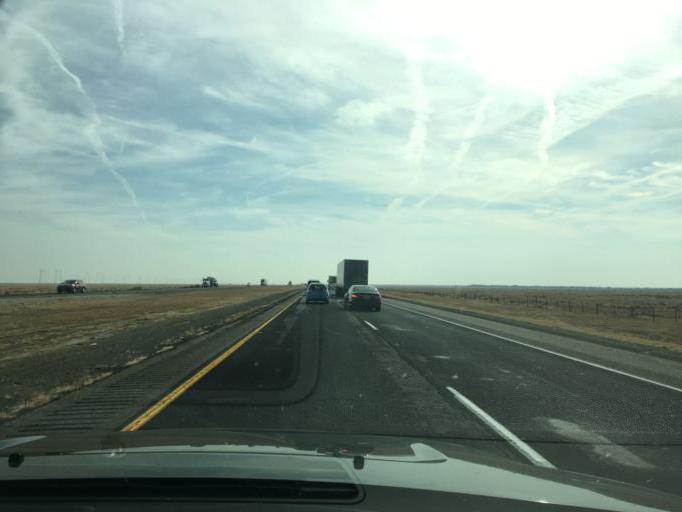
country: US
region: California
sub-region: Kings County
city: Kettleman City
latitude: 35.8296
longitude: -119.8124
